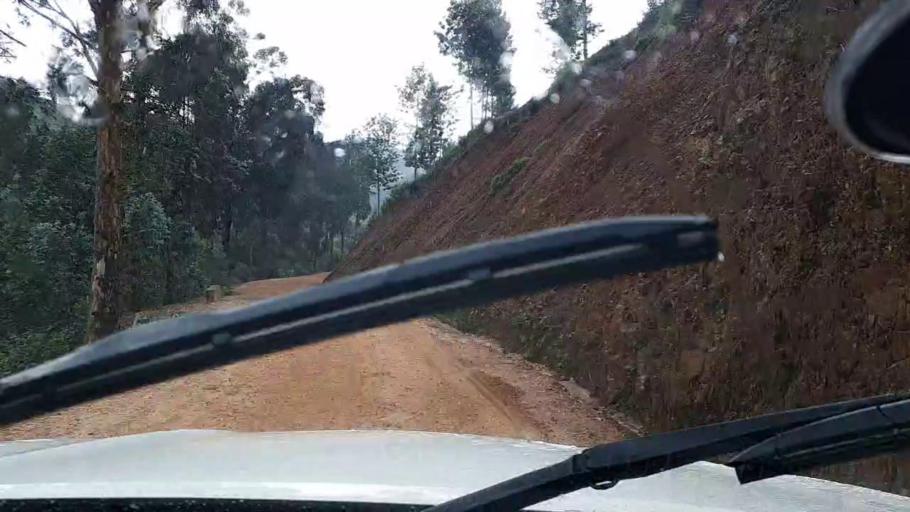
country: RW
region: Western Province
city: Kibuye
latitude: -2.1535
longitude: 29.4296
